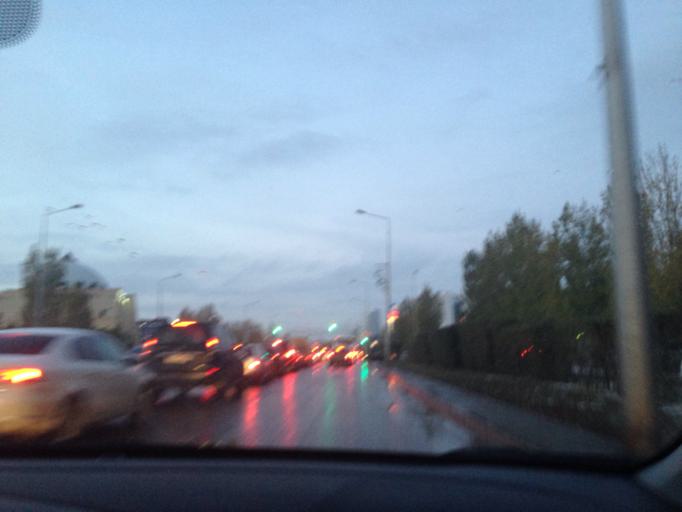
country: KZ
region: Astana Qalasy
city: Astana
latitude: 51.1425
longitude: 71.4109
